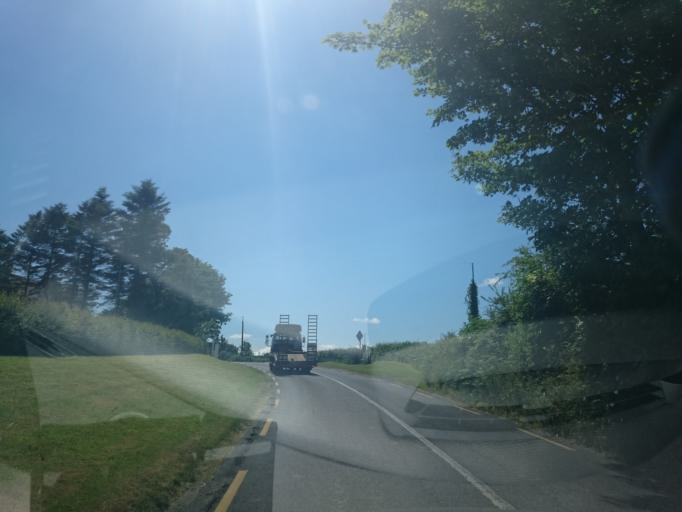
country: IE
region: Leinster
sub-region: Kilkenny
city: Graiguenamanagh
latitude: 52.6001
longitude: -6.9929
